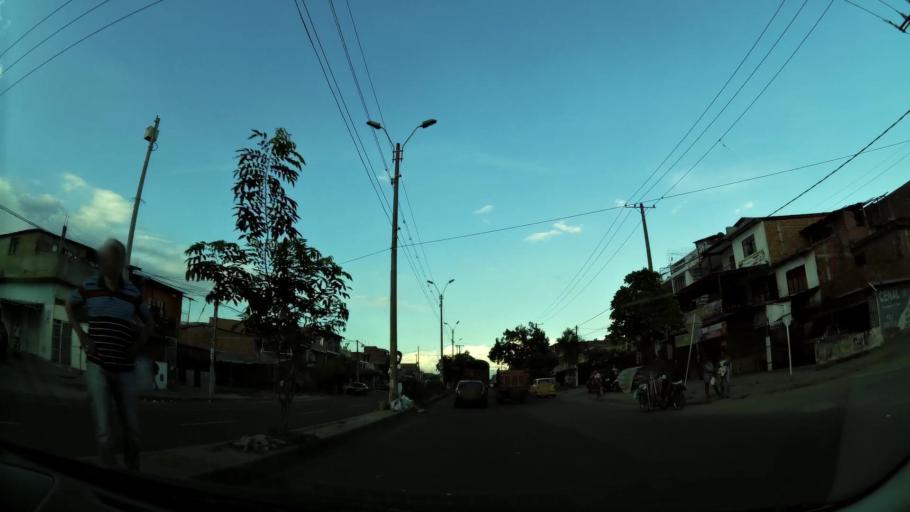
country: CO
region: Valle del Cauca
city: Cali
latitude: 3.4098
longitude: -76.4941
